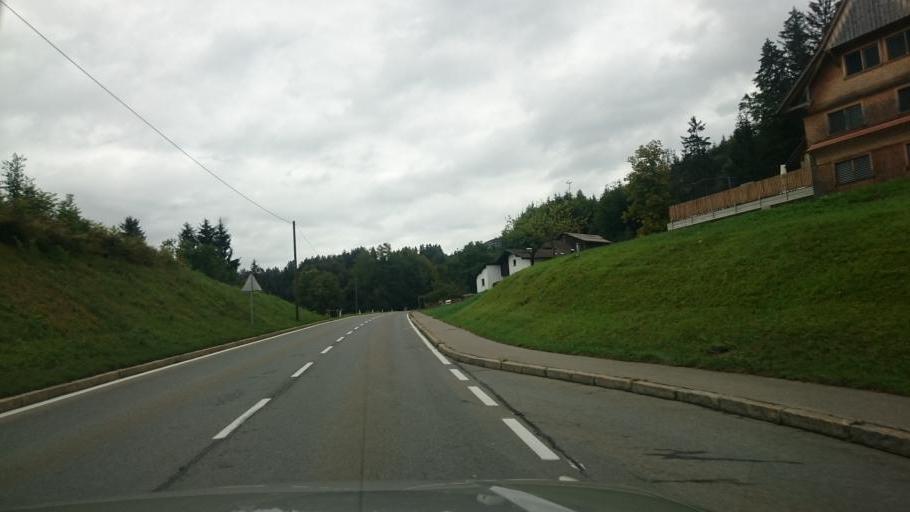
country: AT
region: Vorarlberg
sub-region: Politischer Bezirk Bregenz
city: Bildstein
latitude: 47.4226
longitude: 9.7705
